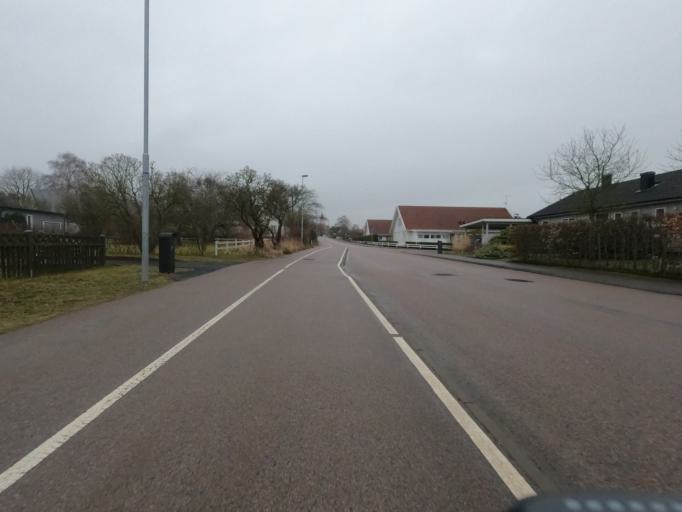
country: SE
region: Halland
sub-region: Halmstads Kommun
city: Fyllinge
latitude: 56.6707
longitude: 12.9068
